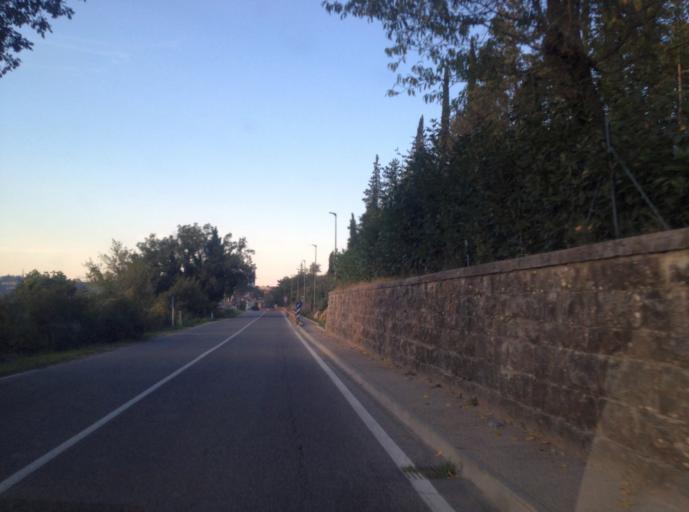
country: IT
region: Tuscany
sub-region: Provincia di Siena
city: Castellina in Chianti
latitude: 43.4593
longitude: 11.2915
